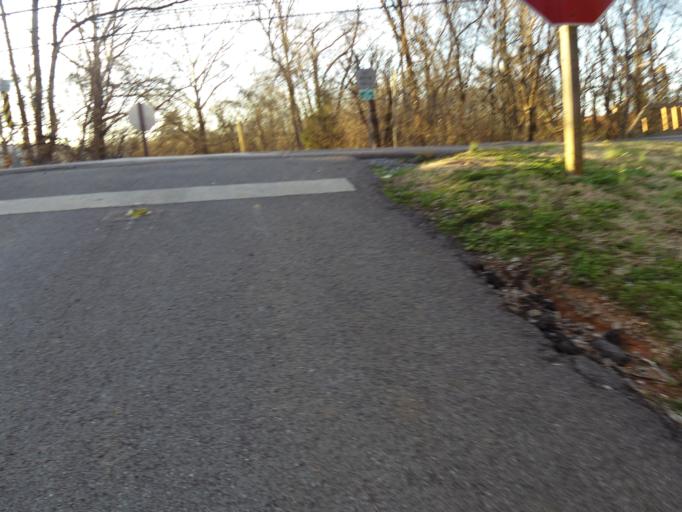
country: US
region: Tennessee
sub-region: Blount County
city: Maryville
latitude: 35.7596
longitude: -83.9793
